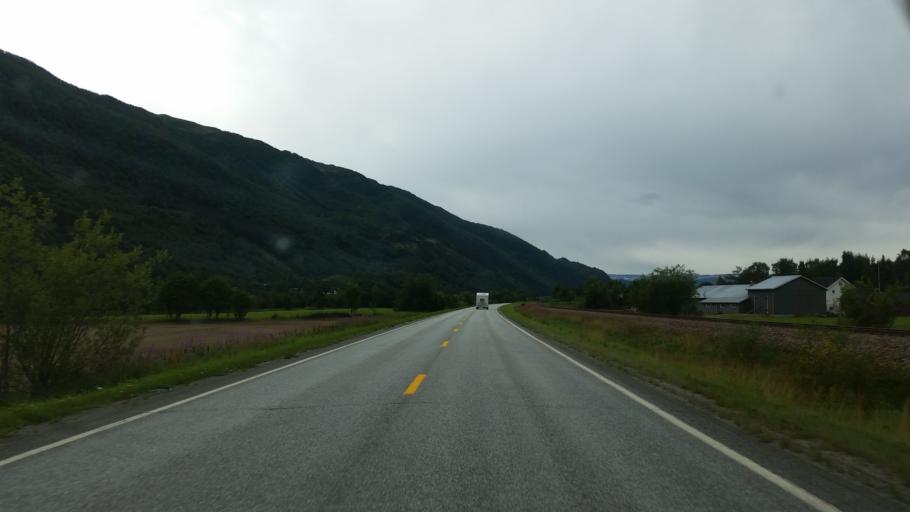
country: NO
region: Nordland
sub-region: Saltdal
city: Rognan
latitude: 67.0524
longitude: 15.3857
